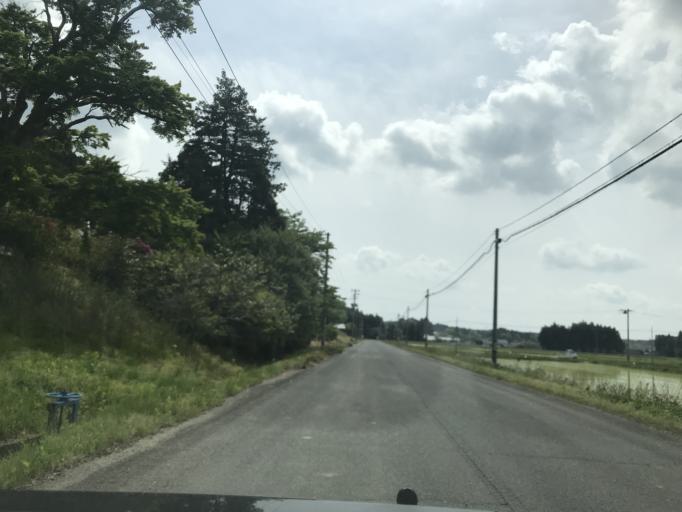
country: JP
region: Iwate
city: Ichinoseki
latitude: 38.8518
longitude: 141.0124
